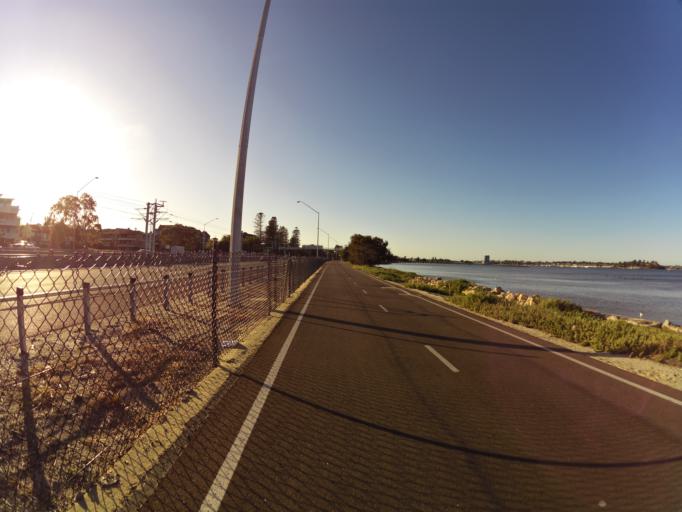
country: AU
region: Western Australia
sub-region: South Perth
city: Como
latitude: -31.9893
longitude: 115.8535
